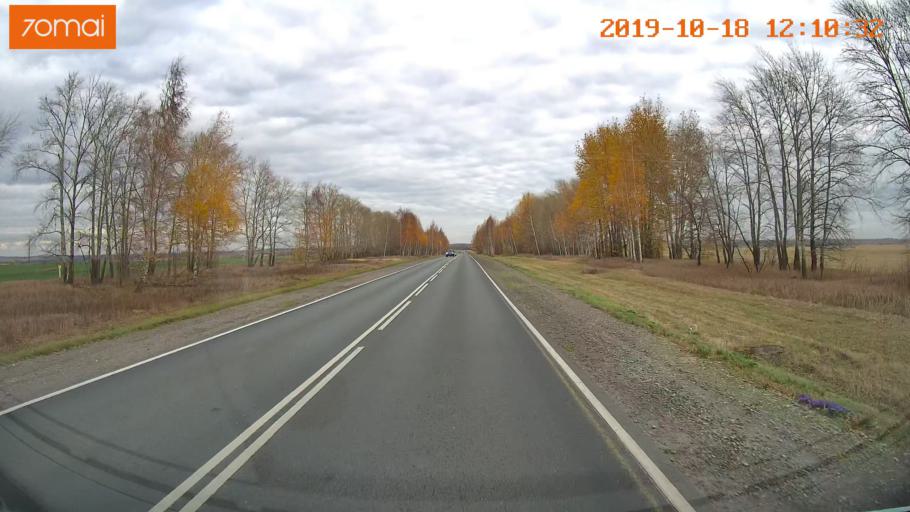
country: RU
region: Rjazan
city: Zakharovo
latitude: 54.3932
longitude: 39.3332
